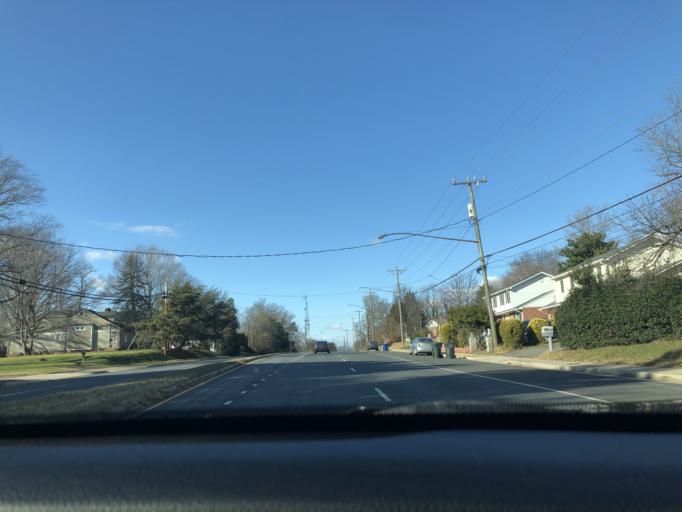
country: US
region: Virginia
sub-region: Fairfax County
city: Burke
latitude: 38.8203
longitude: -77.2773
